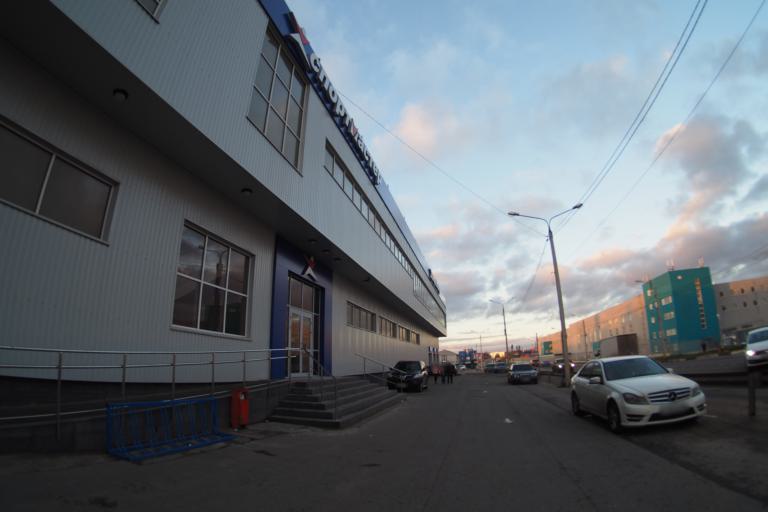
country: RU
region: Moskovskaya
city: Lobnya
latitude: 56.0081
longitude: 37.4372
